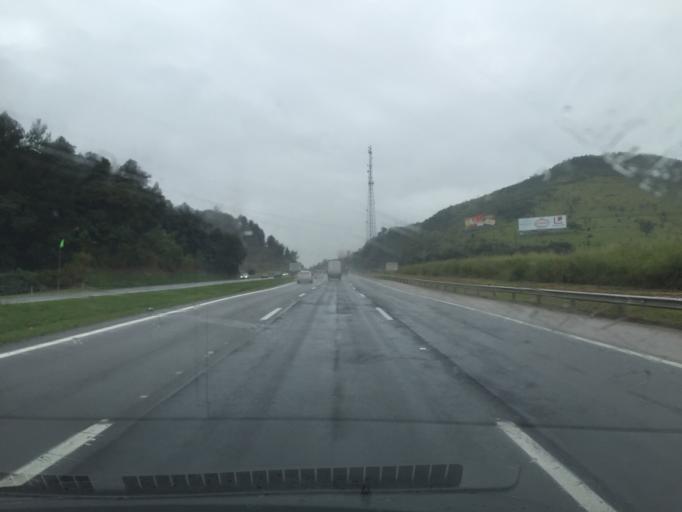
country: BR
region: Sao Paulo
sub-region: Sao Roque
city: Sao Roque
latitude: -23.4336
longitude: -47.1238
